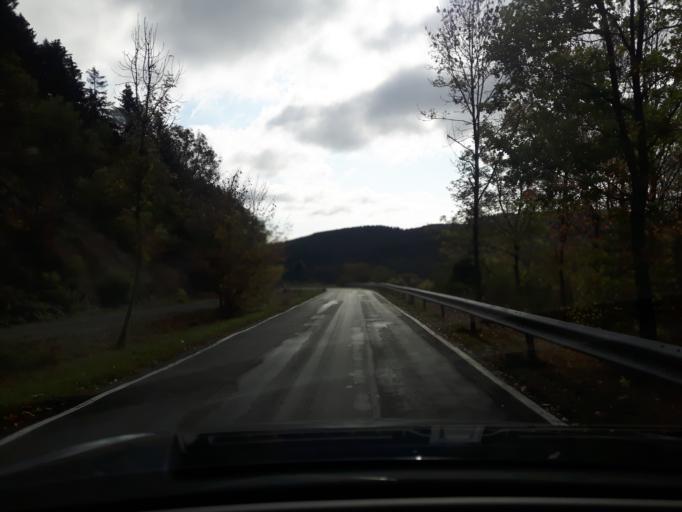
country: DE
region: North Rhine-Westphalia
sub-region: Regierungsbezirk Arnsberg
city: Bad Berleburg
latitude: 51.0227
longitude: 8.4212
